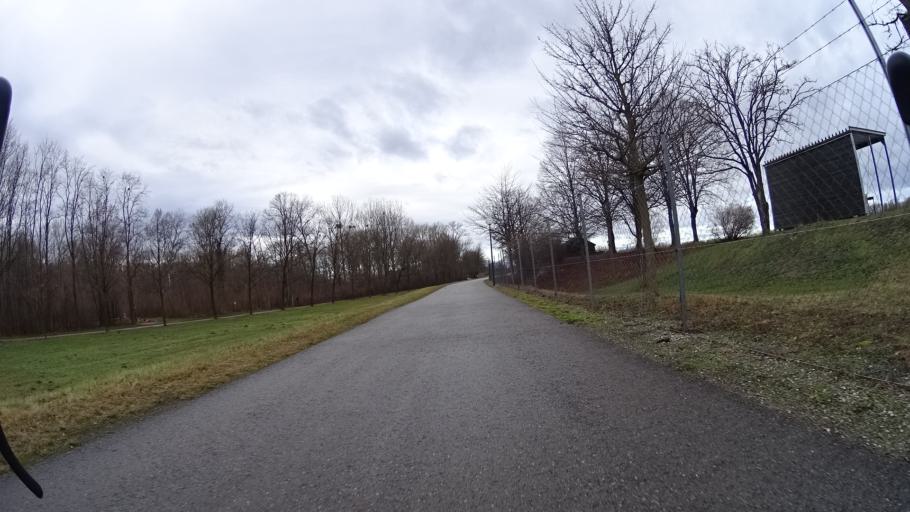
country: AT
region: Lower Austria
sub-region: Politischer Bezirk Tulln
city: Tulln
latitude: 48.3333
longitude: 16.0849
